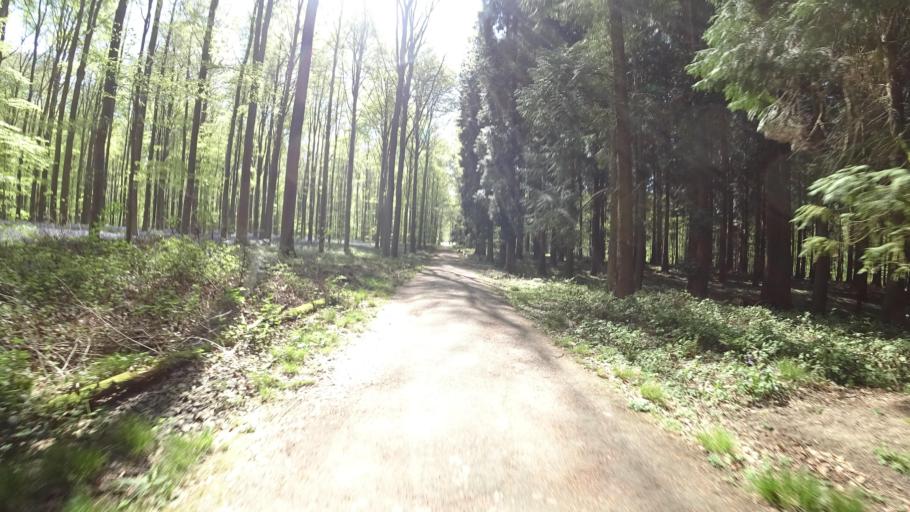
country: BE
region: Wallonia
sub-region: Province du Brabant Wallon
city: Braine-le-Chateau
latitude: 50.7043
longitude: 4.2850
